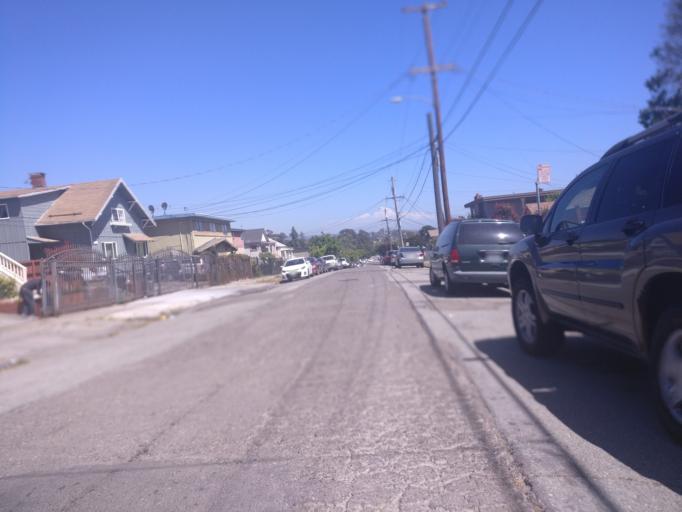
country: US
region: California
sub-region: Alameda County
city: Piedmont
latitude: 37.7927
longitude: -122.2168
